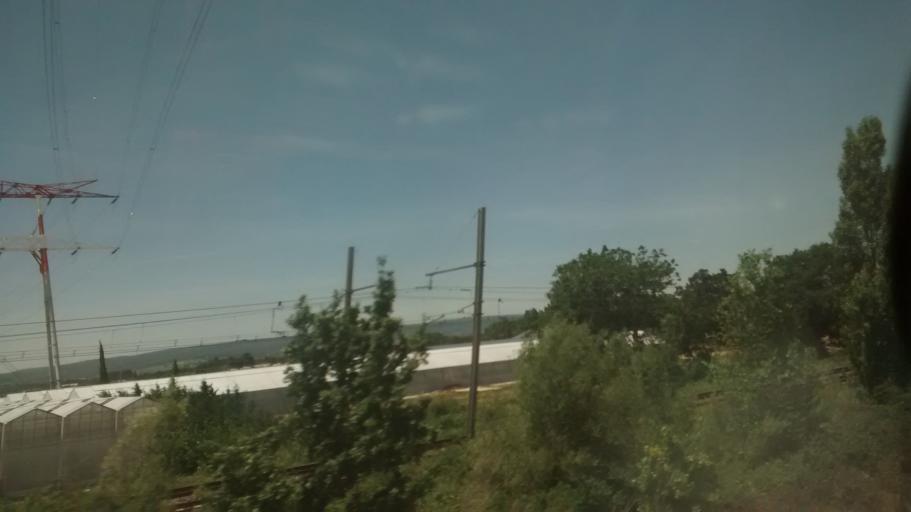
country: FR
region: Provence-Alpes-Cote d'Azur
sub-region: Departement du Vaucluse
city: Lapalud
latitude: 44.3328
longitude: 4.6982
